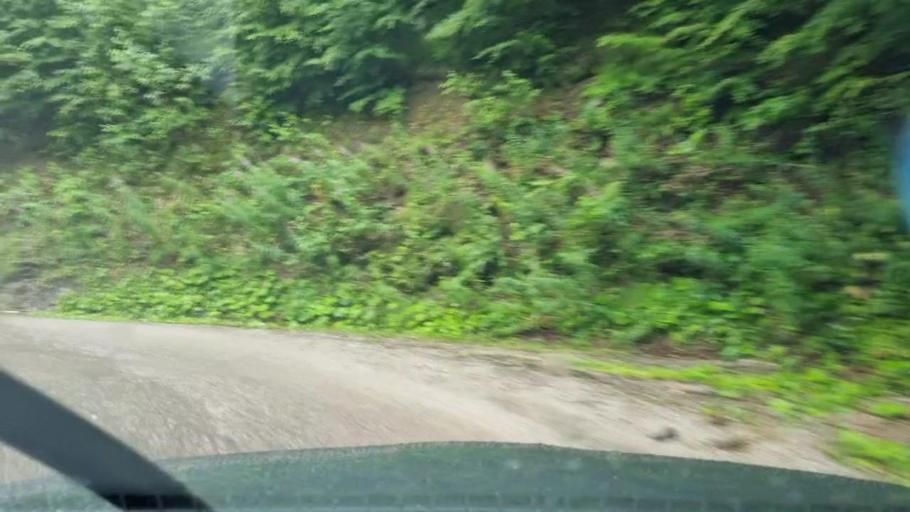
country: BA
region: Republika Srpska
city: Koran
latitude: 43.6424
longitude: 18.6140
